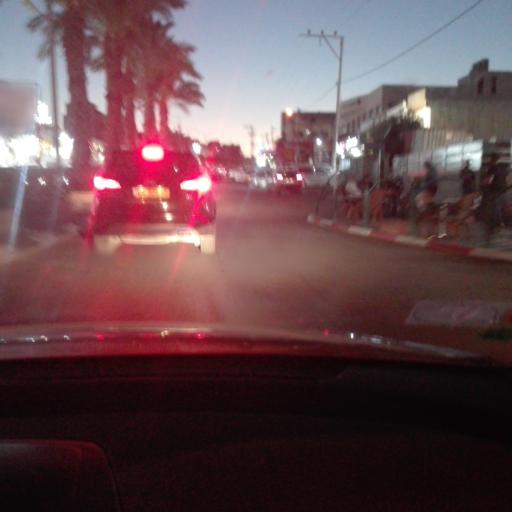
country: PS
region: West Bank
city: Nazlat `Isa
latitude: 32.4206
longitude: 35.0426
